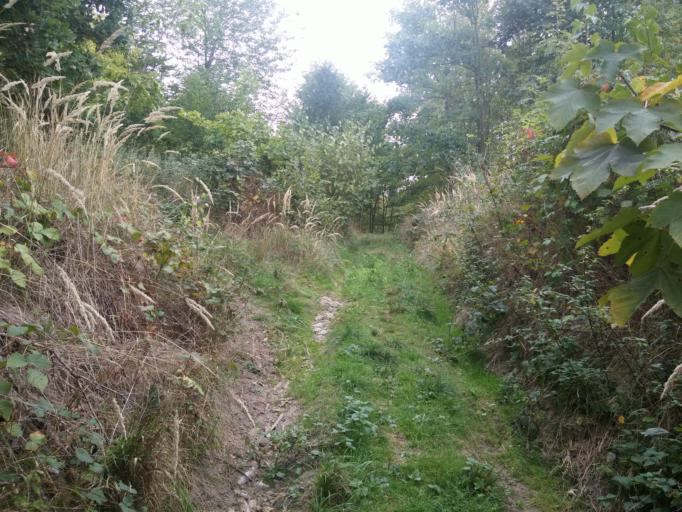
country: CZ
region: Olomoucky
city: Namest' na Hane
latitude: 49.5816
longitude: 17.0184
